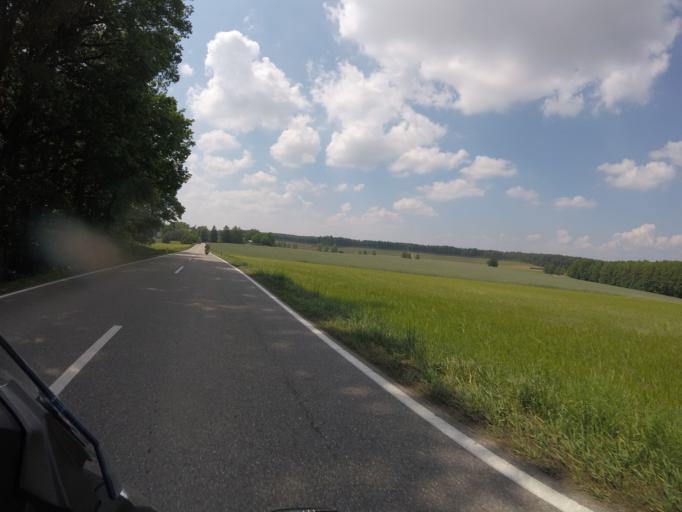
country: DE
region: Bavaria
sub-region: Upper Bavaria
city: Munchsmunster
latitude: 48.7173
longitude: 11.6669
